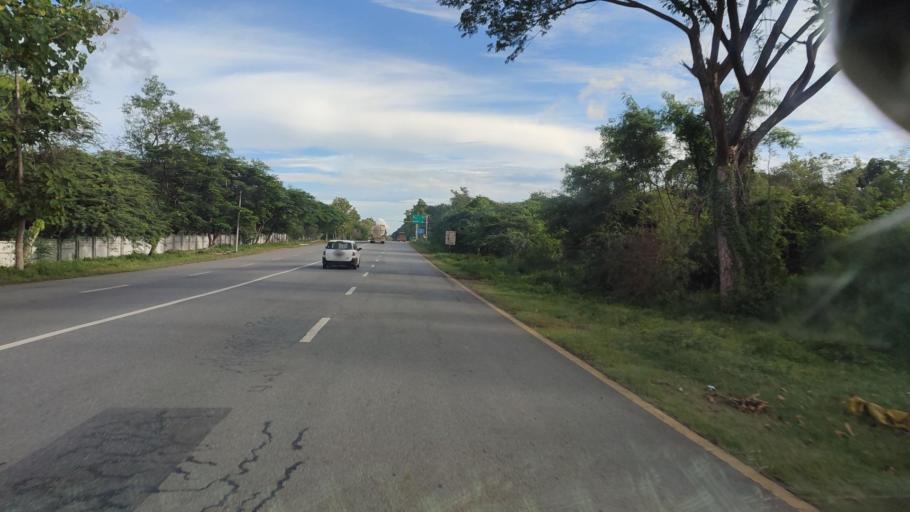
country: MM
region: Mandalay
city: Yamethin
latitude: 20.1610
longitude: 96.1906
